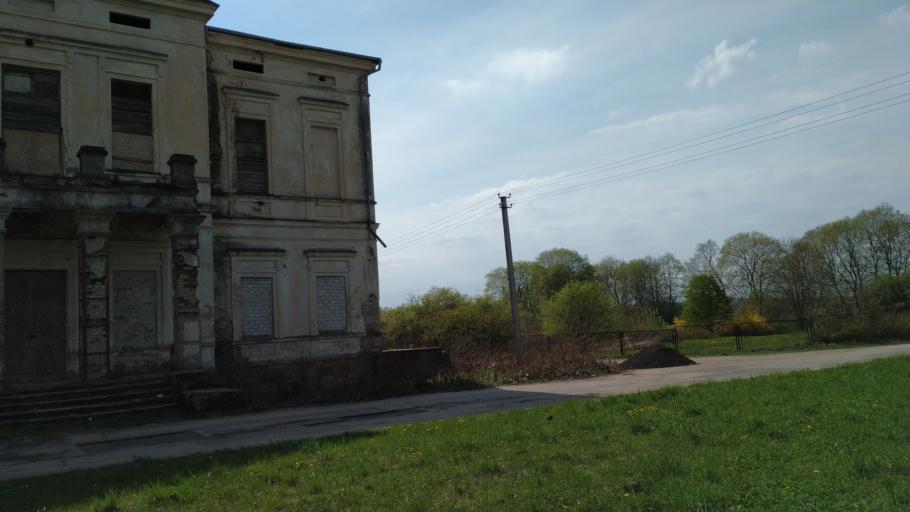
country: LT
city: Baltoji Voke
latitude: 54.5987
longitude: 25.1901
